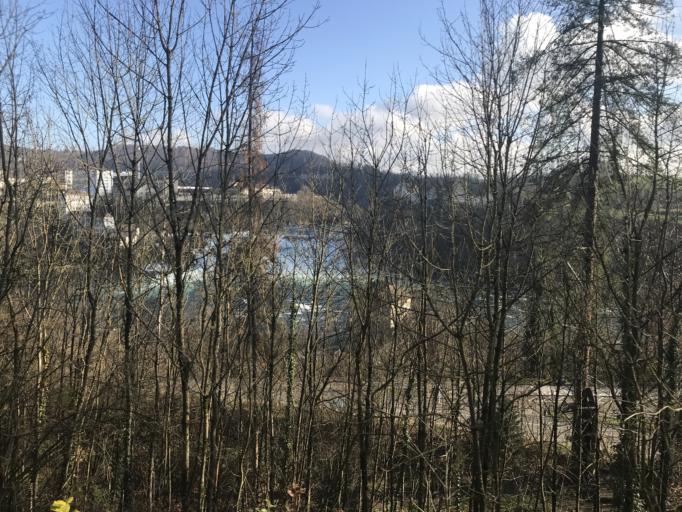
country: CH
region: Schaffhausen
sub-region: Bezirk Schaffhausen
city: Neuhausen
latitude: 47.6788
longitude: 8.6092
